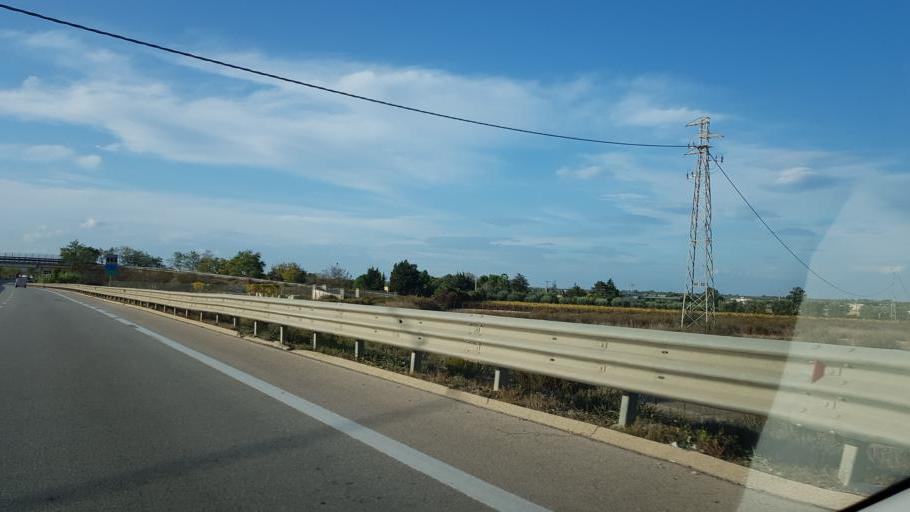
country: IT
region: Apulia
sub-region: Provincia di Brindisi
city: Francavilla Fontana
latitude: 40.5409
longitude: 17.6041
